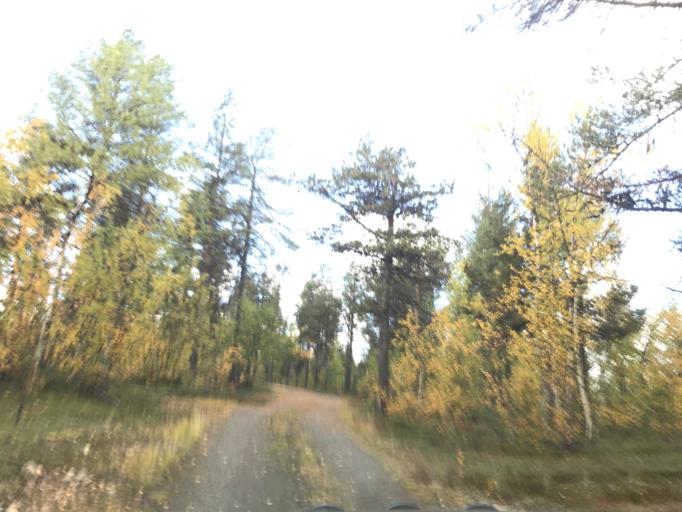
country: SE
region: Norrbotten
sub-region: Gallivare Kommun
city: Malmberget
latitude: 67.5843
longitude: 20.8543
